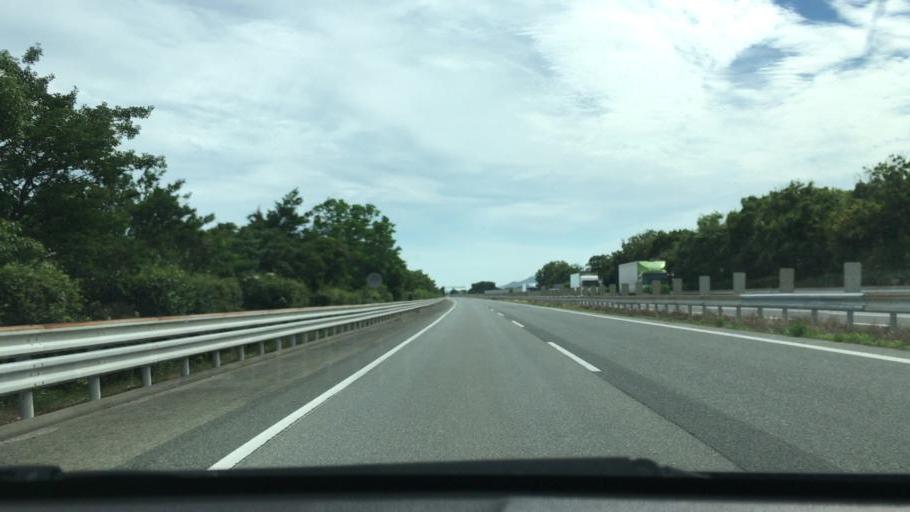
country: JP
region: Yamaguchi
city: Hofu
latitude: 34.0632
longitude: 131.5479
